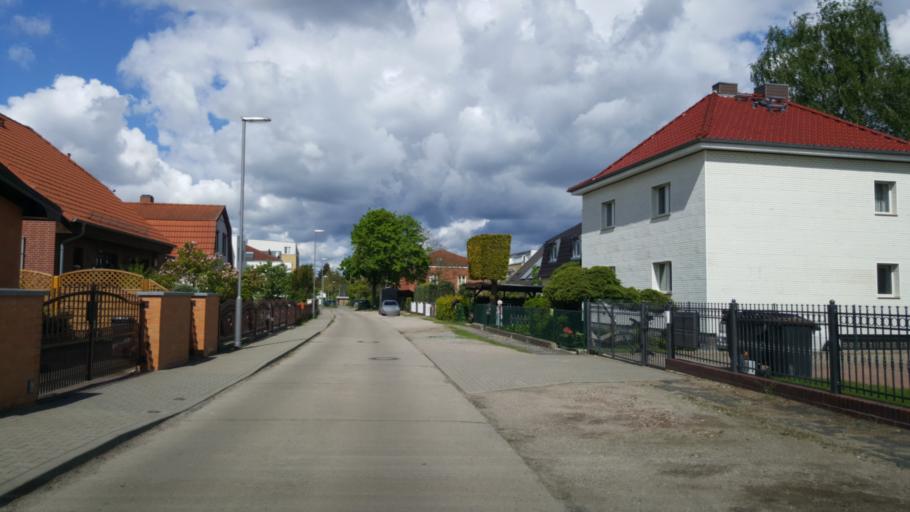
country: DE
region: Berlin
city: Altglienicke
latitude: 52.4183
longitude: 13.5321
